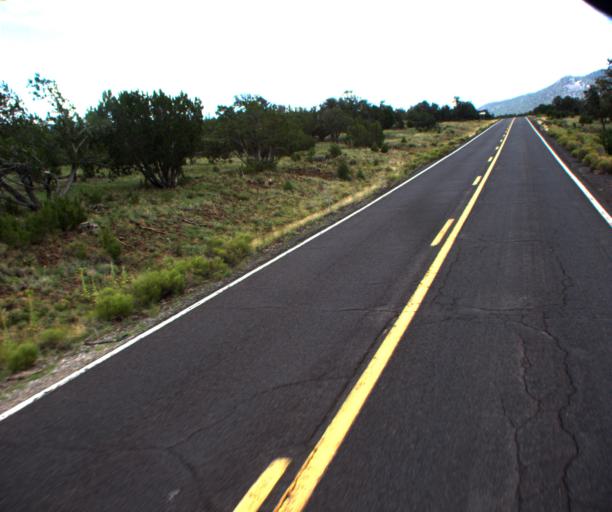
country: US
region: Arizona
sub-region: Coconino County
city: Parks
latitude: 35.5373
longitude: -111.8524
